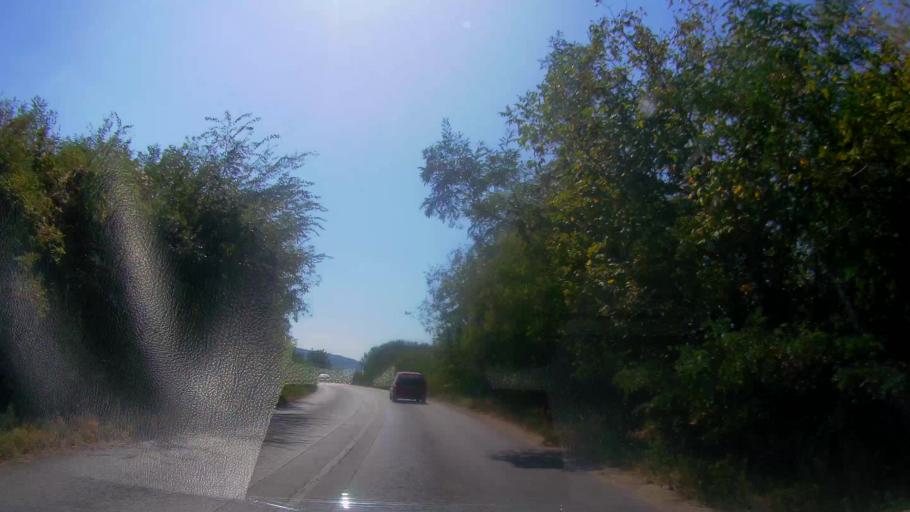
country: BG
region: Veliko Turnovo
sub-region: Obshtina Gorna Oryakhovitsa
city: Purvomaytsi
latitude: 43.1663
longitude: 25.6172
